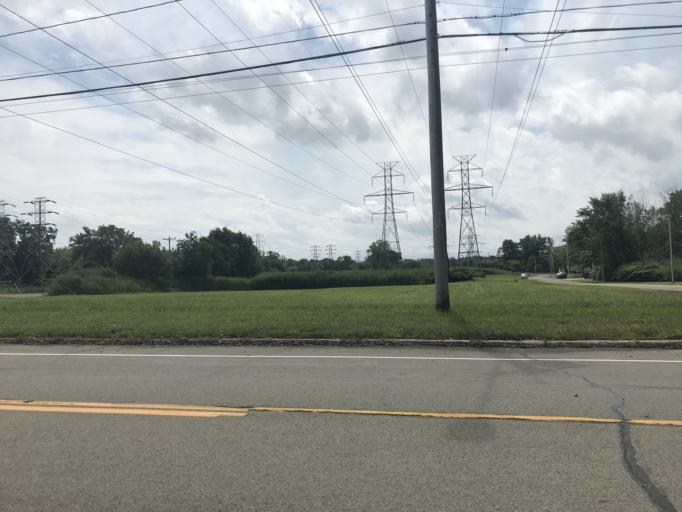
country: US
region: New York
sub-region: Chautauqua County
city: Dunkirk
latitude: 42.4849
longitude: -79.3512
